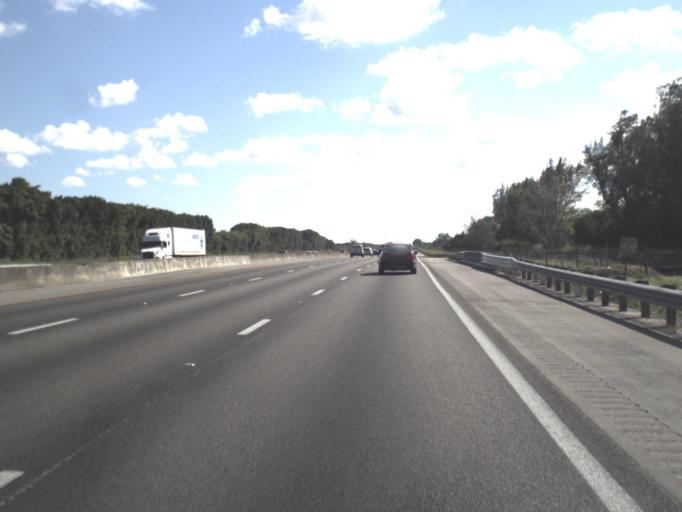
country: US
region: Florida
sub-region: Palm Beach County
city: Kings Point
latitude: 26.4246
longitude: -80.1718
